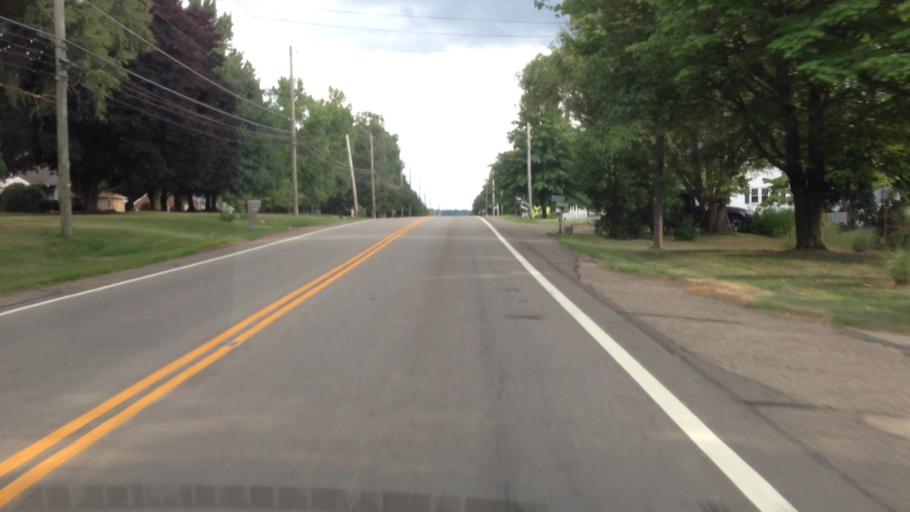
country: US
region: Ohio
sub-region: Summit County
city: Lakemore
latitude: 41.0131
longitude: -81.4636
